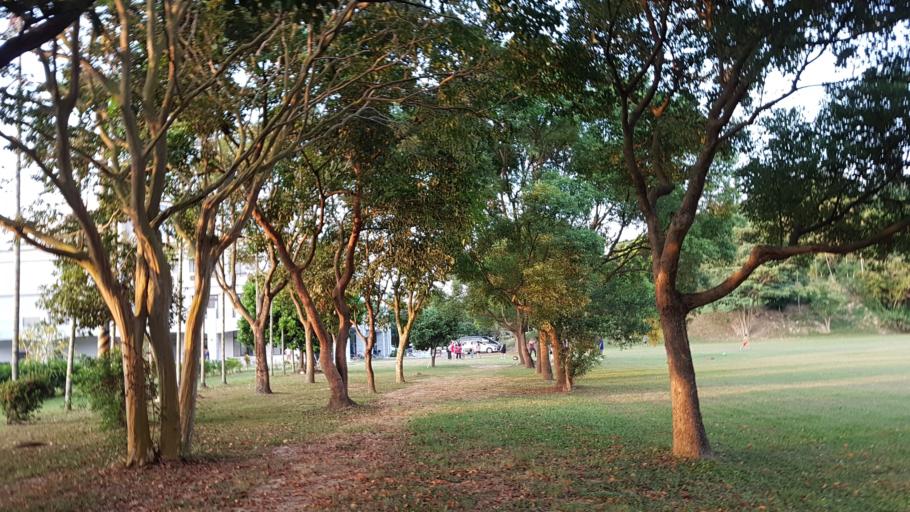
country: TW
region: Taiwan
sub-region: Chiayi
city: Jiayi Shi
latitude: 23.3583
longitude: 120.4673
